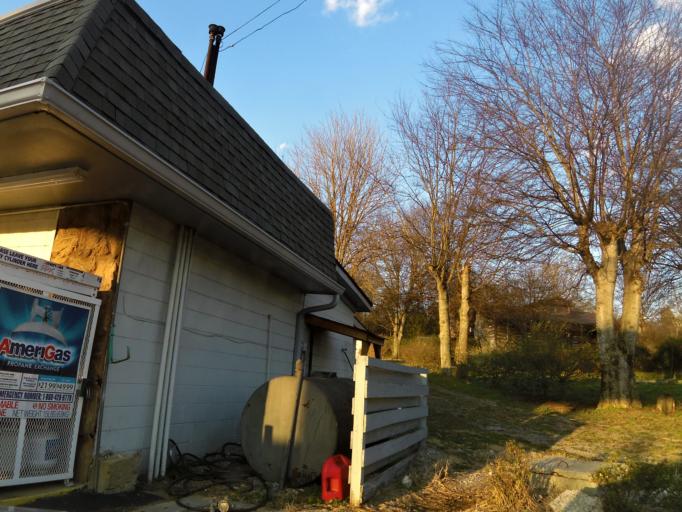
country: US
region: Tennessee
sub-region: Wilson County
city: Mount Juliet
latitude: 36.2320
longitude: -86.4909
